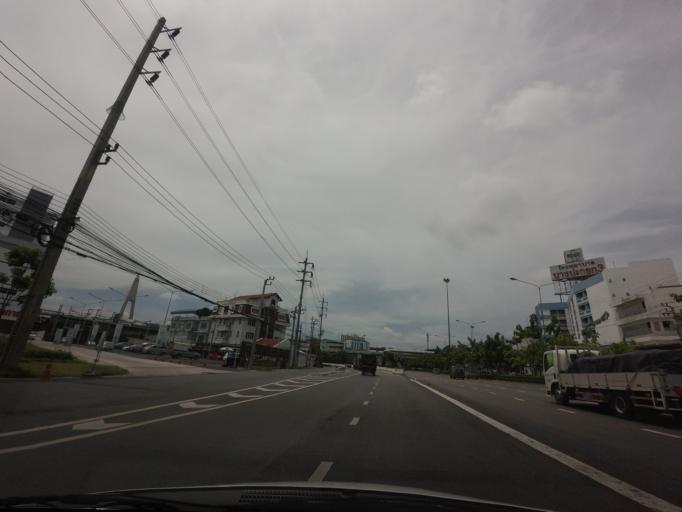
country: TH
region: Bangkok
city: Thung Khru
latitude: 13.6353
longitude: 100.5286
